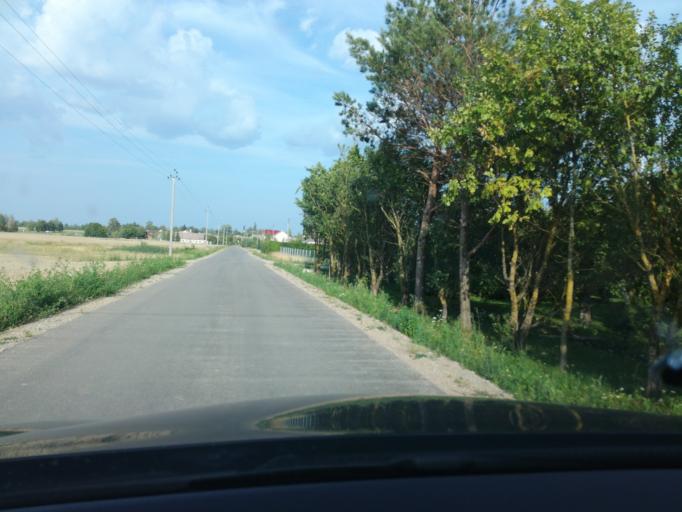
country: LT
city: Simnas
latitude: 54.3850
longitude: 23.6779
